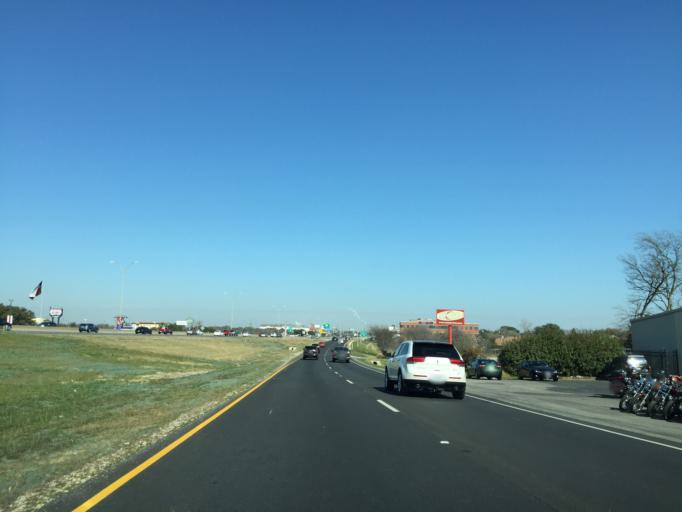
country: US
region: Texas
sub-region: Williamson County
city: Round Rock
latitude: 30.5202
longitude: -97.6881
